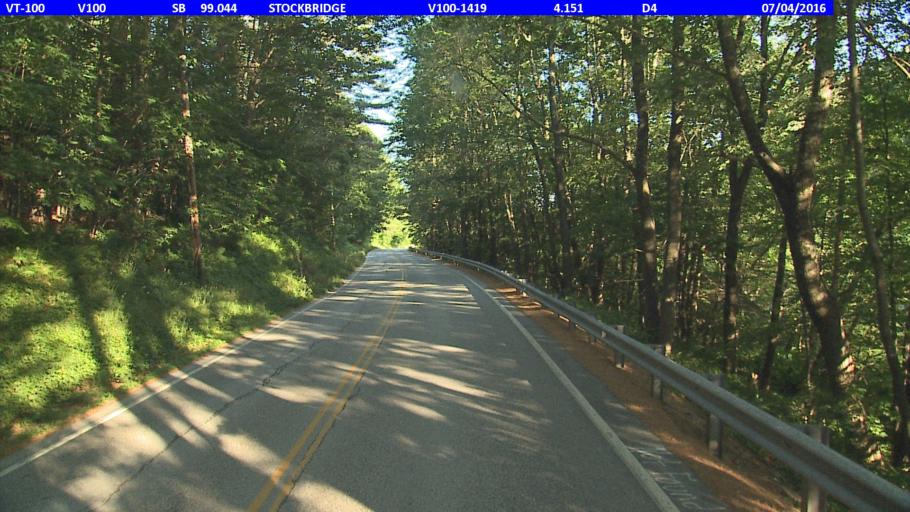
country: US
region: Vermont
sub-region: Orange County
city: Randolph
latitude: 43.7966
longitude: -72.7684
